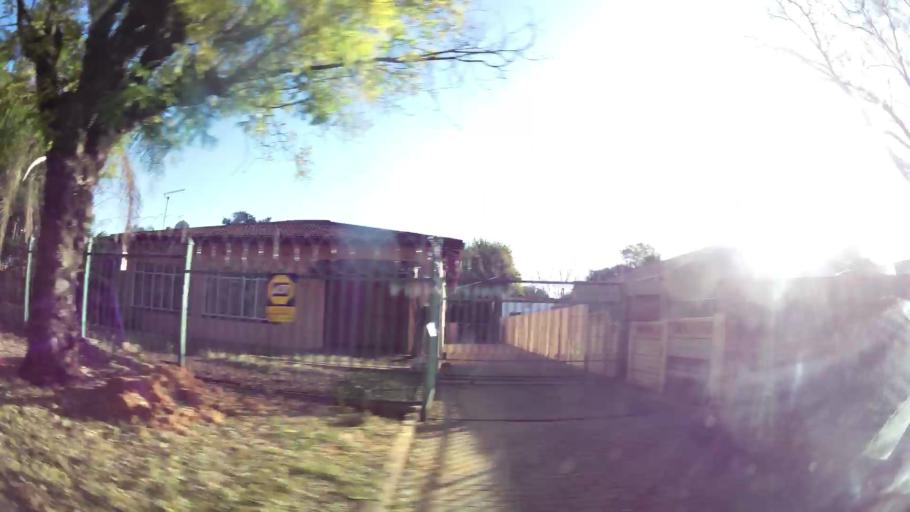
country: ZA
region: Gauteng
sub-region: City of Tshwane Metropolitan Municipality
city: Pretoria
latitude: -25.7114
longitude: 28.2059
